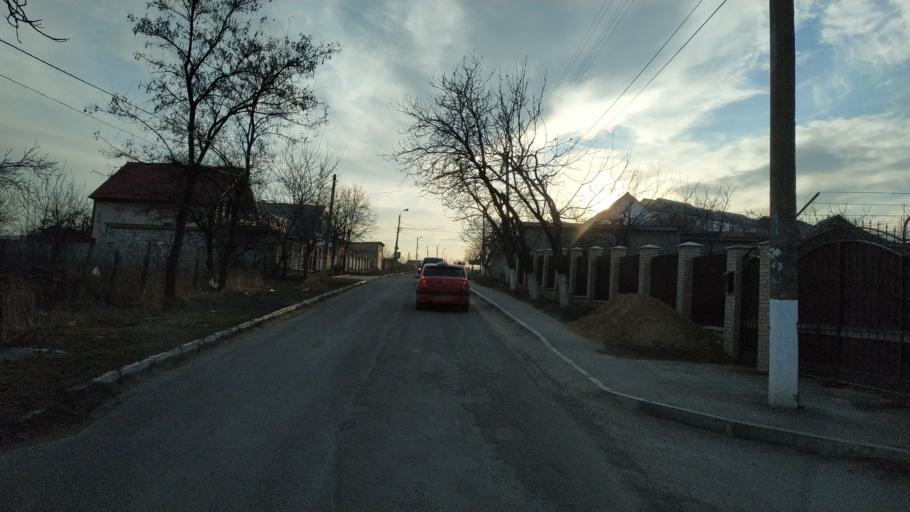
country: MD
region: Nisporeni
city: Nisporeni
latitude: 47.0865
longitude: 28.1721
